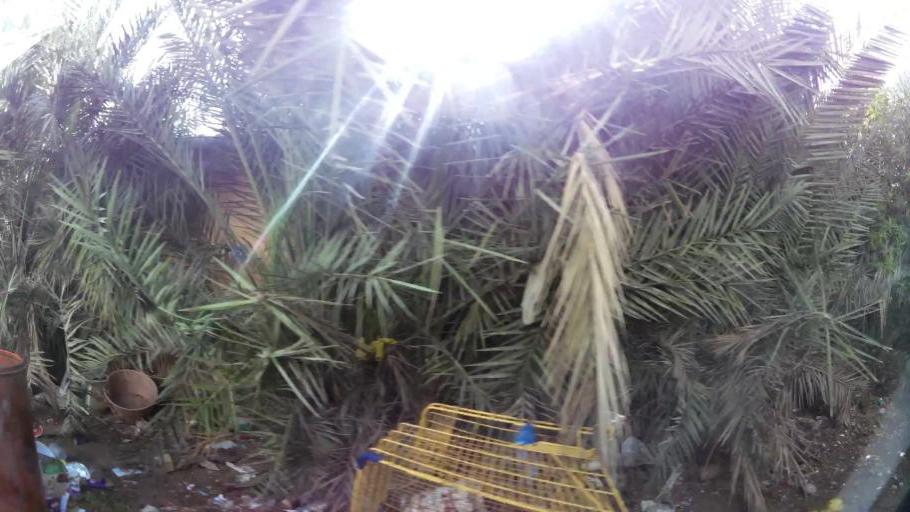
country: AE
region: Ajman
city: Ajman
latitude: 25.4078
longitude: 55.4495
